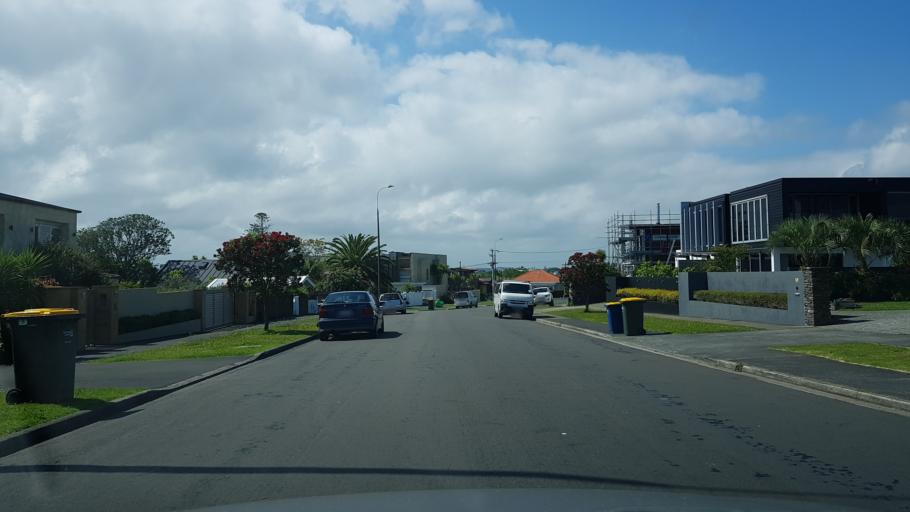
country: NZ
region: Auckland
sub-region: Auckland
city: North Shore
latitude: -36.8109
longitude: 174.7986
